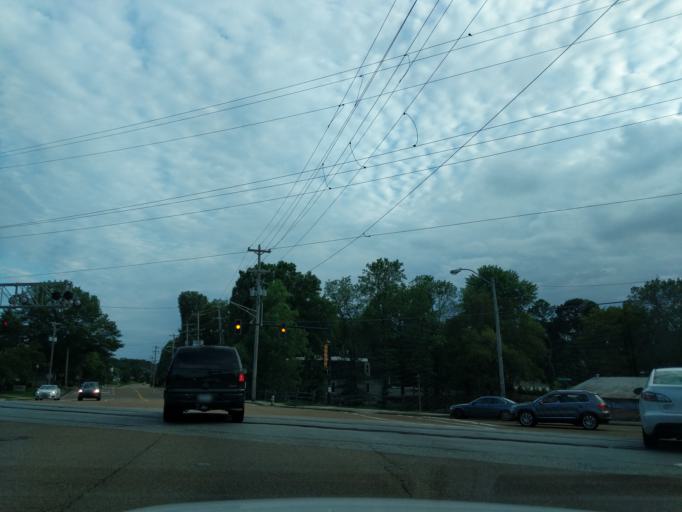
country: US
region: Tennessee
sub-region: Shelby County
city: Germantown
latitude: 35.0879
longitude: -89.8118
